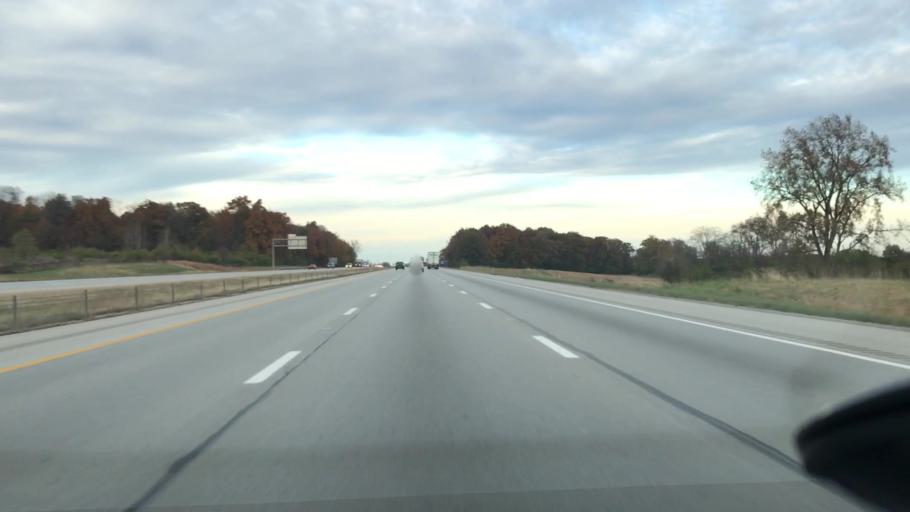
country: US
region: Ohio
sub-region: Clark County
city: Lisbon
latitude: 39.9076
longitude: -83.7101
